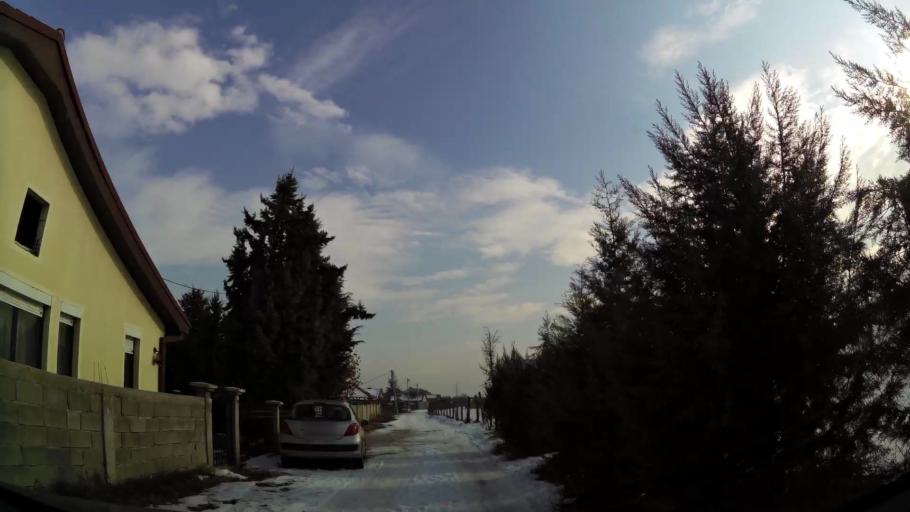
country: MK
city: Creshevo
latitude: 42.0101
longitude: 21.4956
